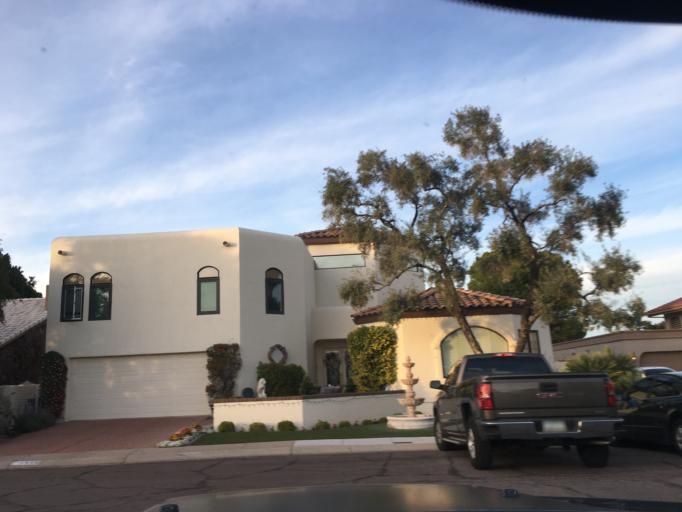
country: US
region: Arizona
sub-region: Maricopa County
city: Tempe
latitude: 33.3760
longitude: -111.9156
